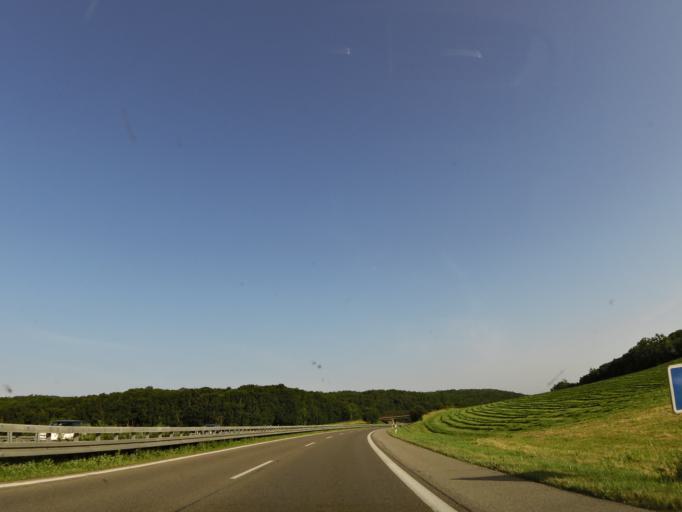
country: DE
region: Baden-Wuerttemberg
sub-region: Regierungsbezirk Stuttgart
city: Hohenstadt
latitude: 48.5349
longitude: 9.6542
